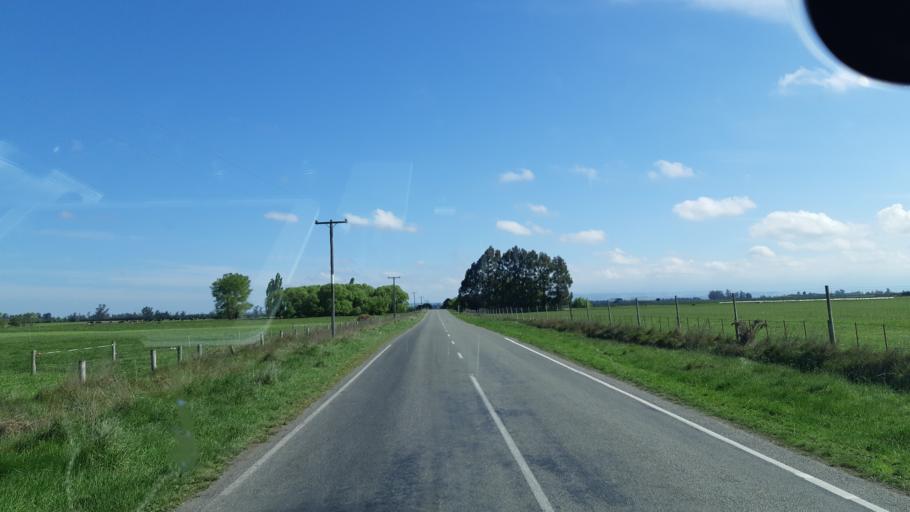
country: NZ
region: Canterbury
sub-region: Timaru District
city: Pleasant Point
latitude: -44.2217
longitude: 171.1835
